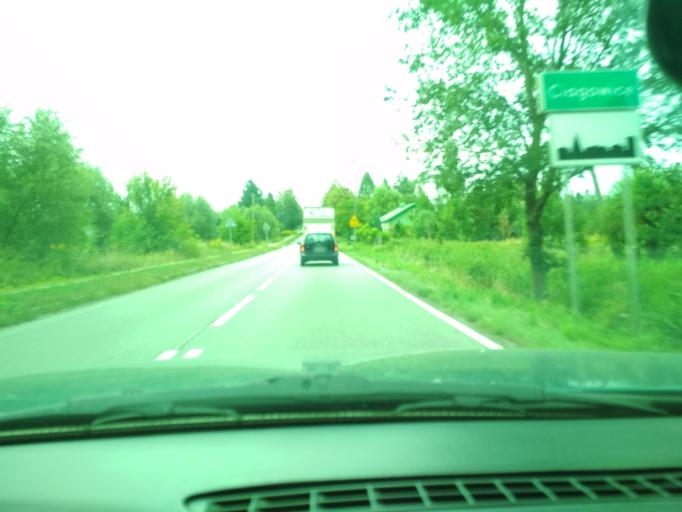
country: PL
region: Silesian Voivodeship
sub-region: Powiat zawiercianski
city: Wysoka
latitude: 50.4420
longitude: 19.3576
